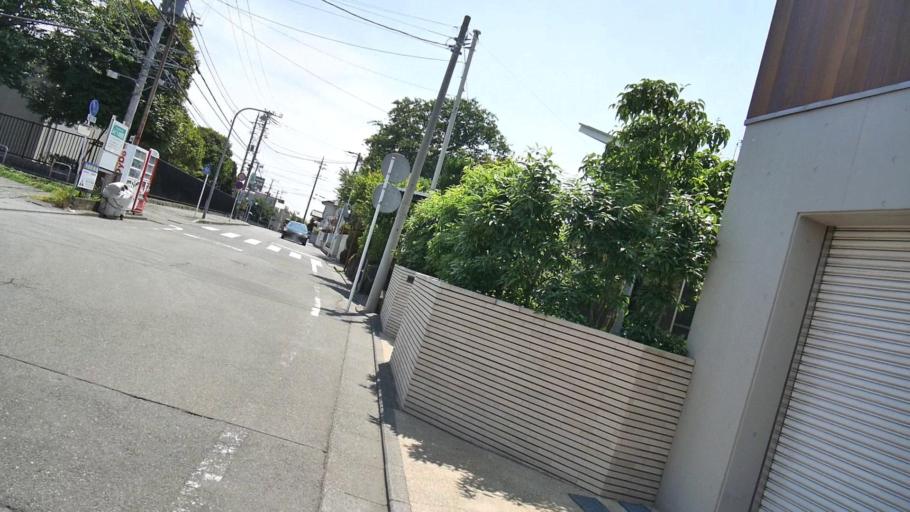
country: JP
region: Kanagawa
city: Fujisawa
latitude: 35.4007
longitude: 139.5164
